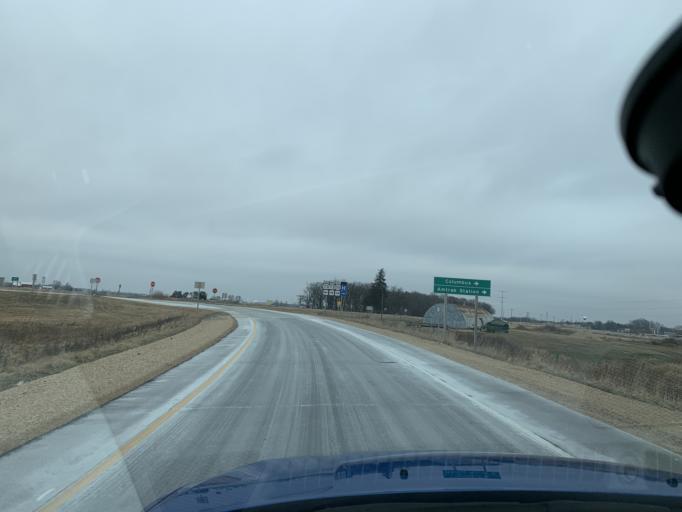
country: US
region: Wisconsin
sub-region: Columbia County
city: Columbus
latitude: 43.3172
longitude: -89.0440
